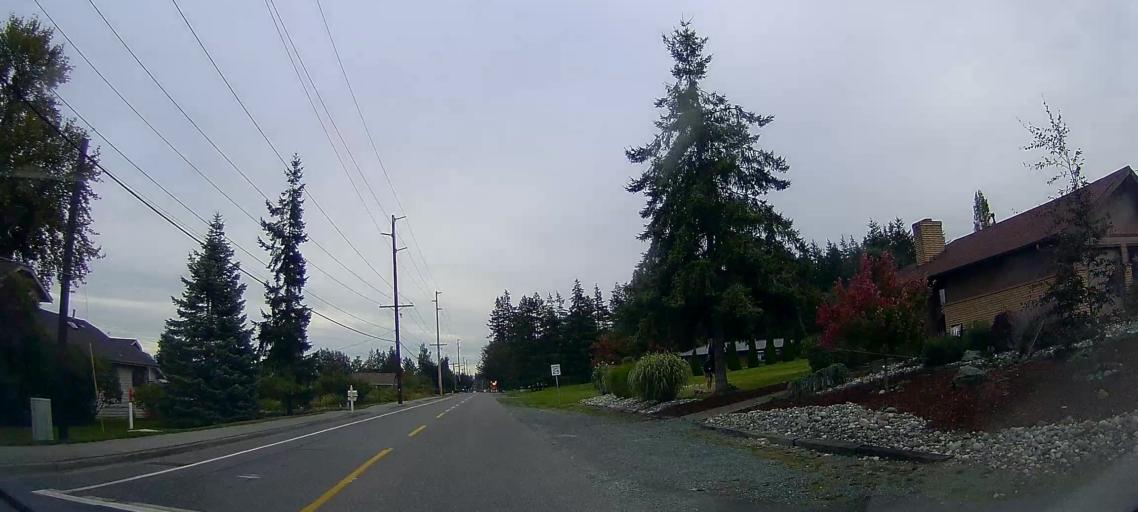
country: US
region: Washington
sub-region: Skagit County
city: Anacortes
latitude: 48.4880
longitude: -122.6251
